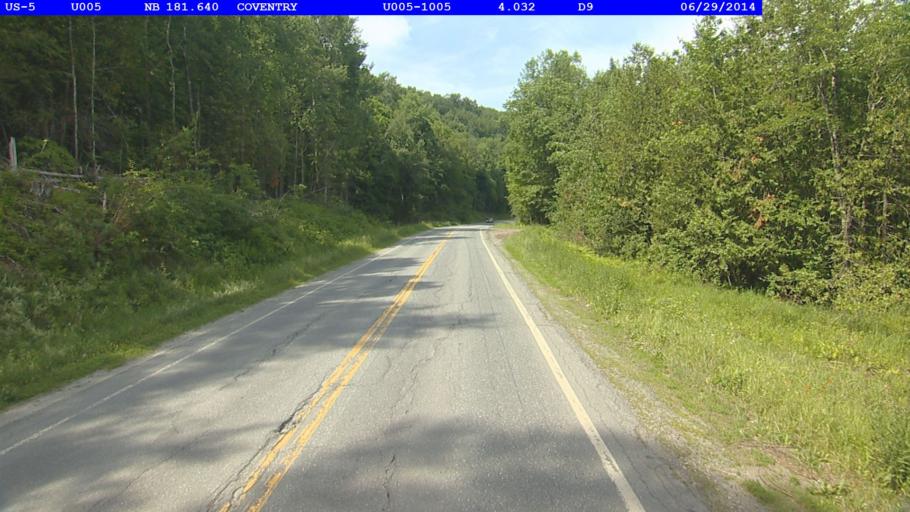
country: US
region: Vermont
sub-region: Orleans County
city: Newport
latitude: 44.9128
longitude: -72.2388
